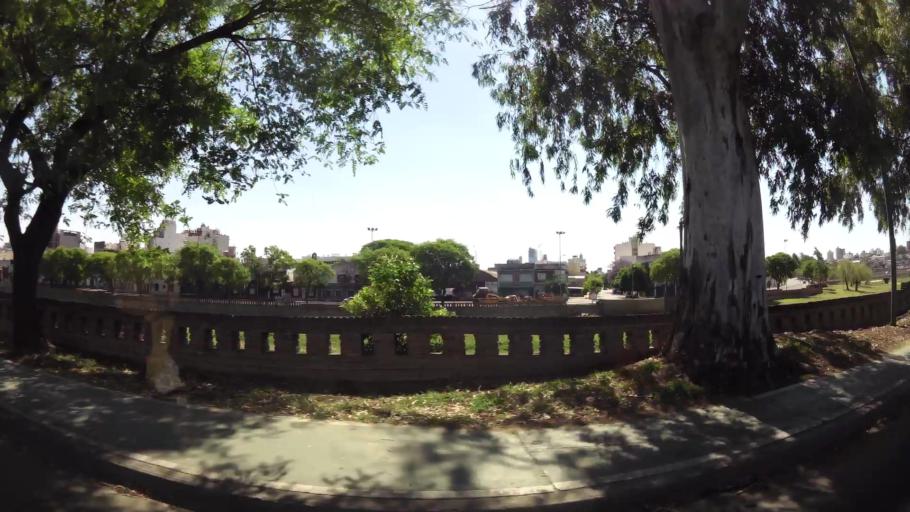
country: AR
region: Cordoba
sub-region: Departamento de Capital
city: Cordoba
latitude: -31.4100
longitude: -64.1745
